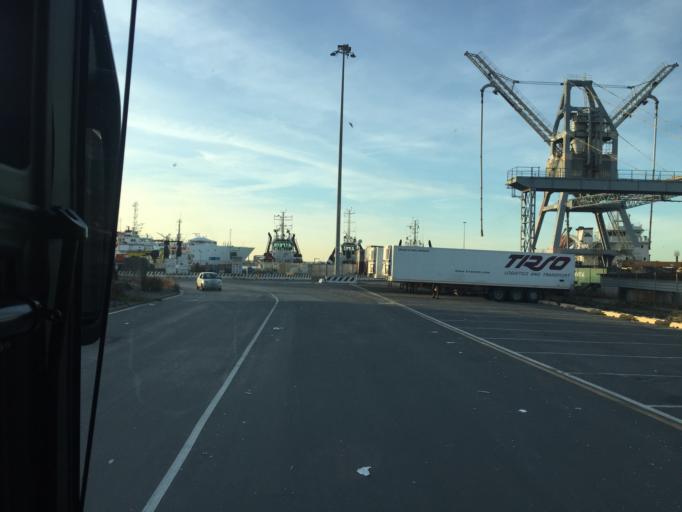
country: IT
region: Tuscany
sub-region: Provincia di Livorno
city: Livorno
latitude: 43.5611
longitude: 10.3042
